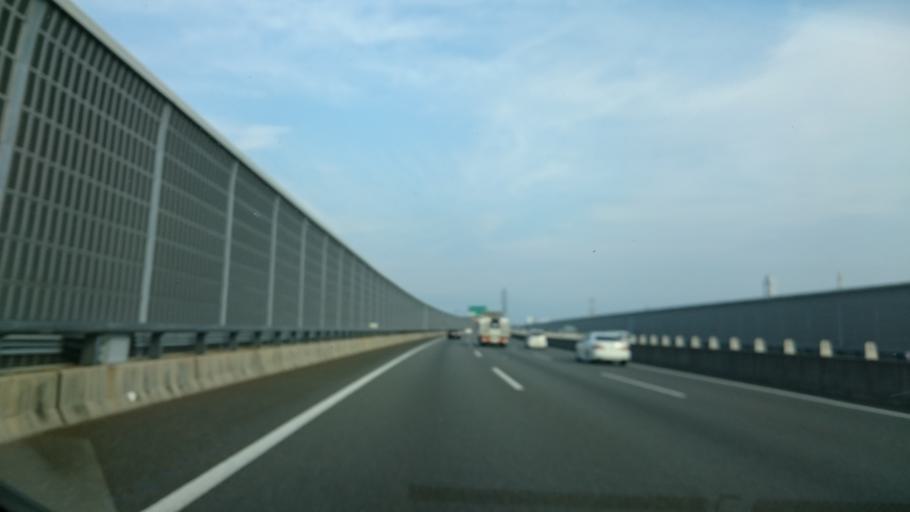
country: JP
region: Mie
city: Yokkaichi
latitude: 35.0271
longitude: 136.6762
